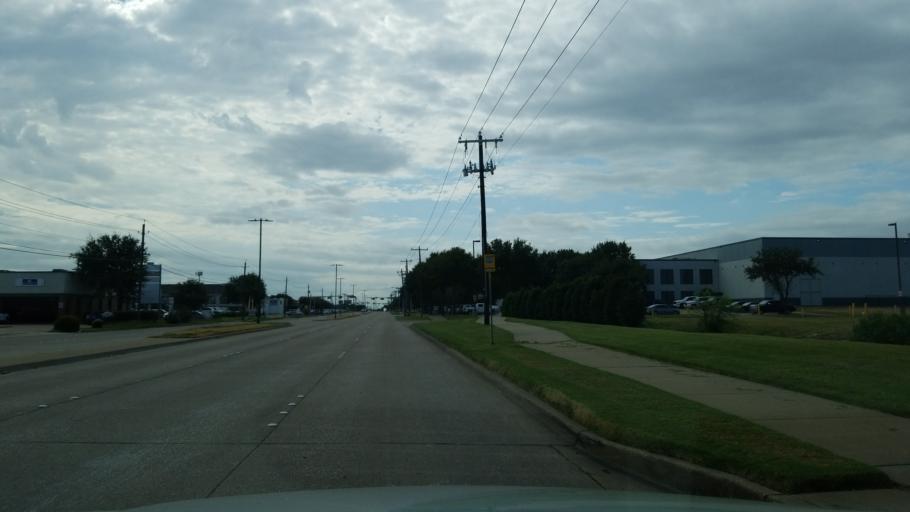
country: US
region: Texas
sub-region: Dallas County
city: Garland
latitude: 32.8914
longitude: -96.6831
